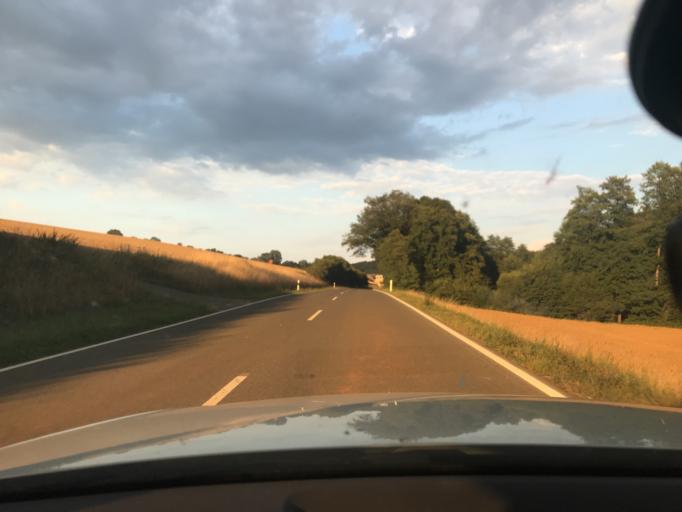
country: DE
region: Bavaria
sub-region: Upper Palatinate
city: Auerbach
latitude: 49.7470
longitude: 11.6092
